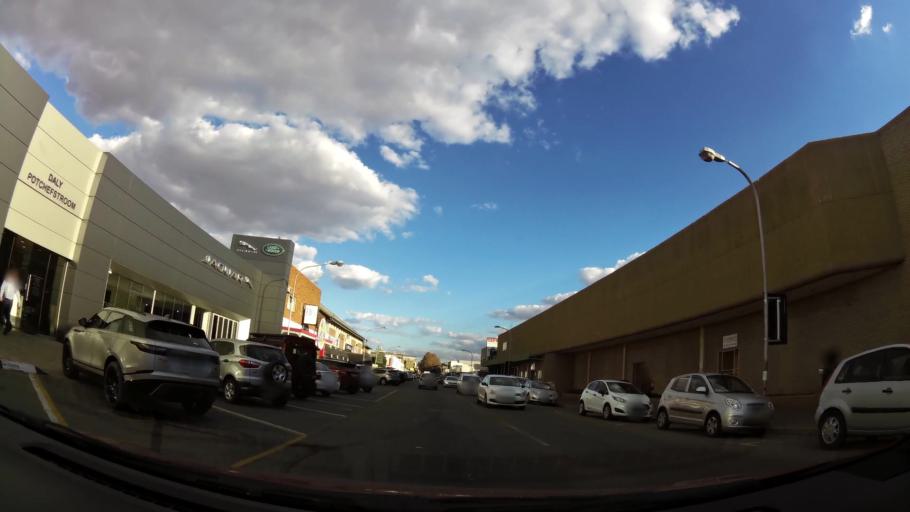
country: ZA
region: North-West
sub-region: Dr Kenneth Kaunda District Municipality
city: Potchefstroom
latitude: -26.7084
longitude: 27.0976
